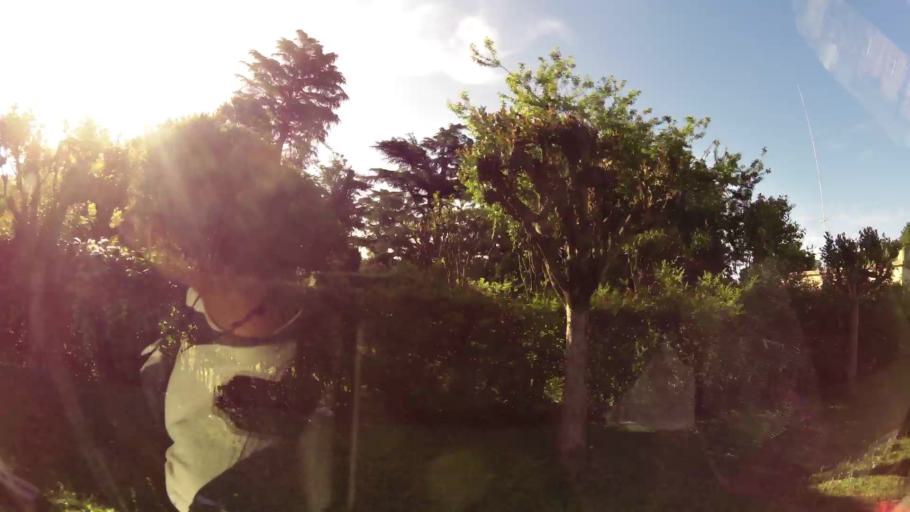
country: AR
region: Buenos Aires
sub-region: Partido de Quilmes
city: Quilmes
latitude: -34.8159
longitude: -58.2167
